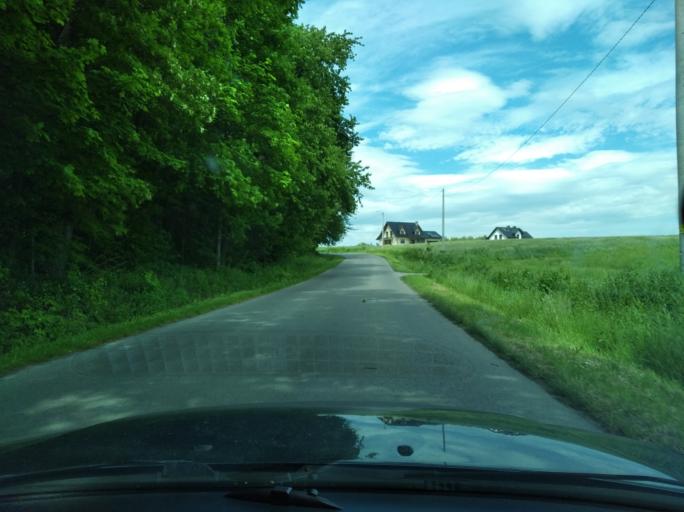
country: PL
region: Subcarpathian Voivodeship
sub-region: Powiat ropczycko-sedziszowski
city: Ropczyce
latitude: 50.0058
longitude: 21.6140
